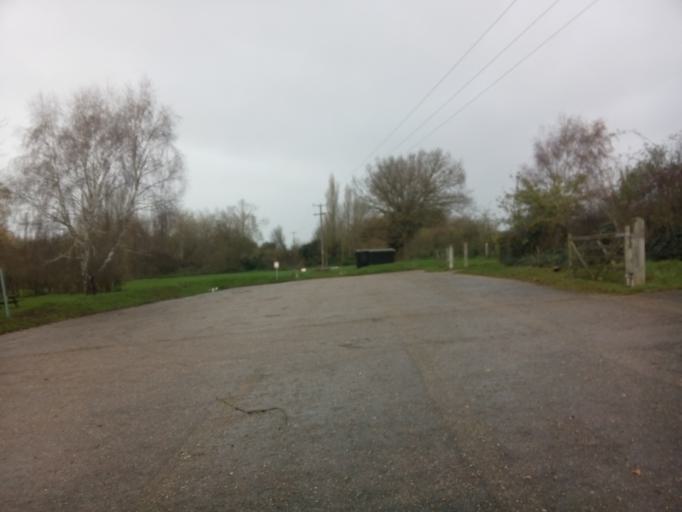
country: GB
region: England
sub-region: Suffolk
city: Needham Market
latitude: 52.1515
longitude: 1.0614
